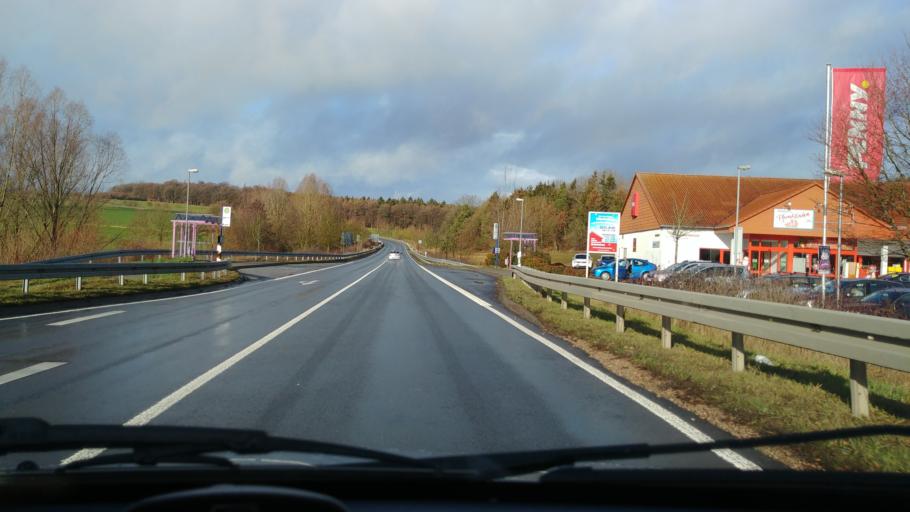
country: DE
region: Hesse
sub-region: Regierungsbezirk Darmstadt
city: Idstein
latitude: 50.1750
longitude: 8.2173
